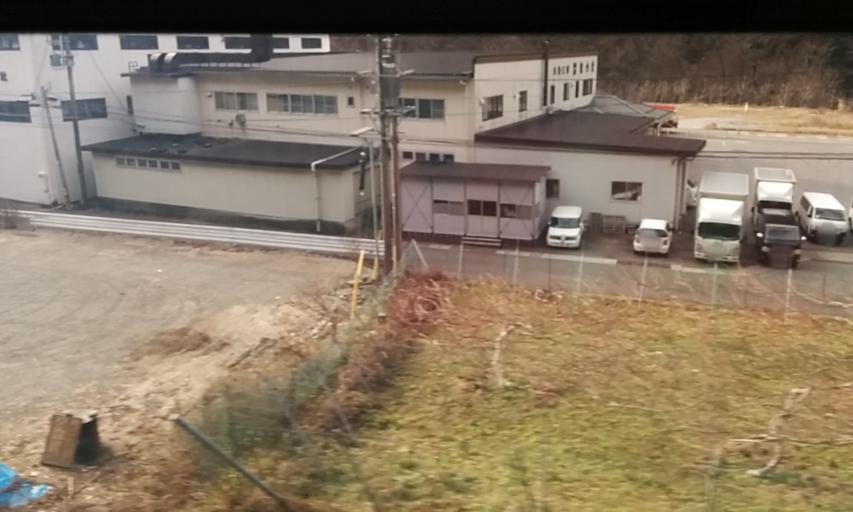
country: JP
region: Nagano
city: Tatsuno
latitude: 35.9938
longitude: 137.8522
